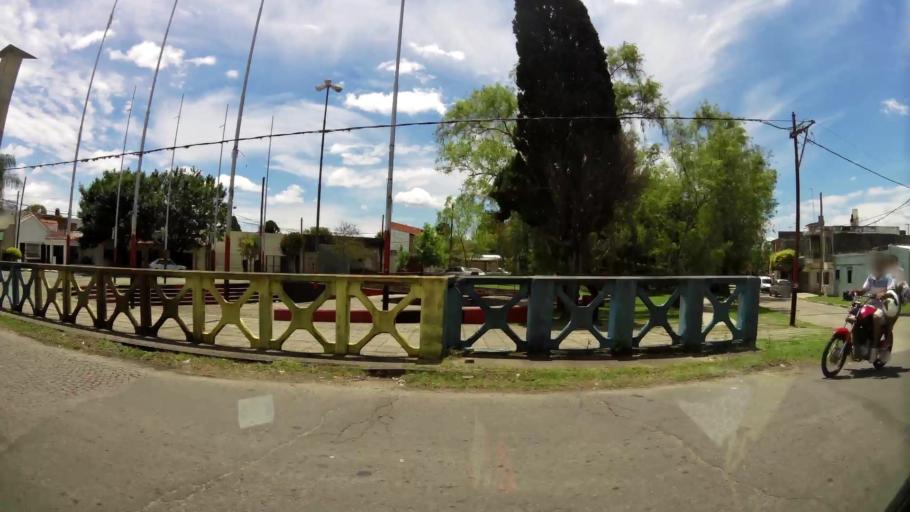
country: AR
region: Santa Fe
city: Gobernador Galvez
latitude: -33.0023
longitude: -60.6247
